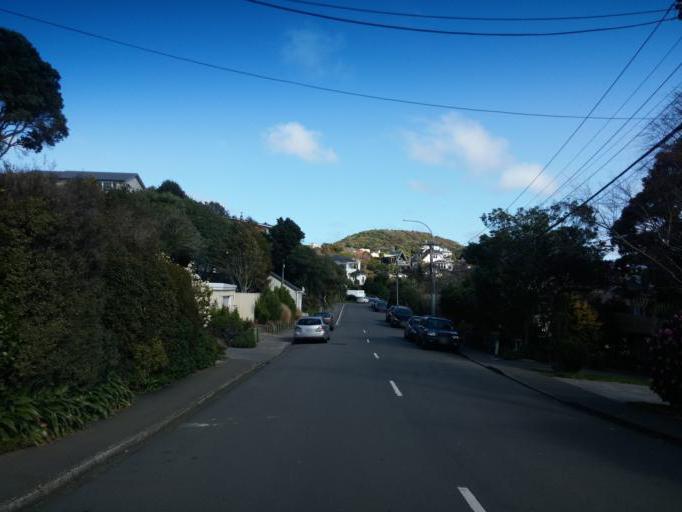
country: NZ
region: Wellington
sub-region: Wellington City
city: Wellington
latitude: -41.2480
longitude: 174.7894
